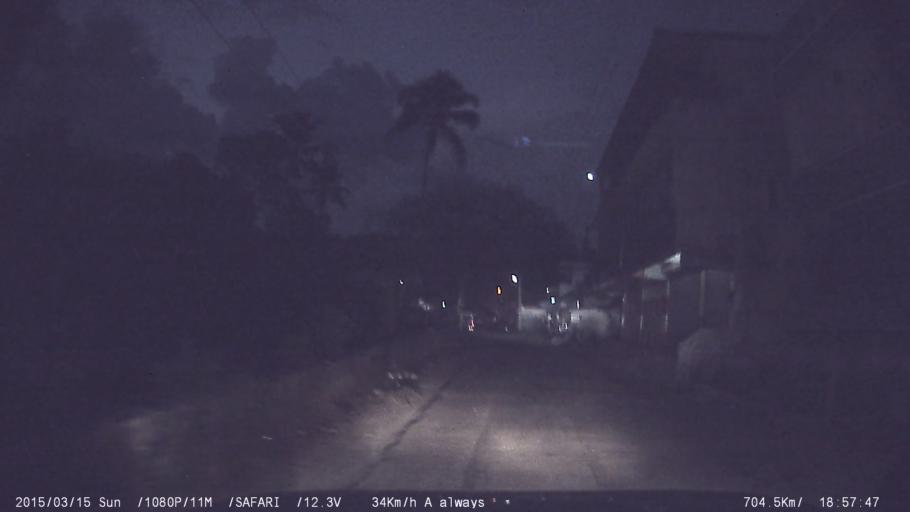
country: IN
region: Kerala
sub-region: Kottayam
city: Palackattumala
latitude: 9.8676
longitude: 76.6685
